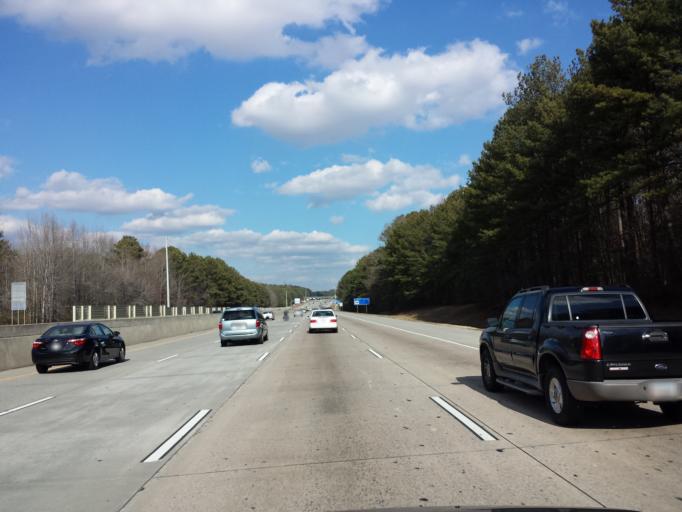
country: US
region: Georgia
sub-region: Fulton County
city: Alpharetta
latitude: 34.0961
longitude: -84.2527
